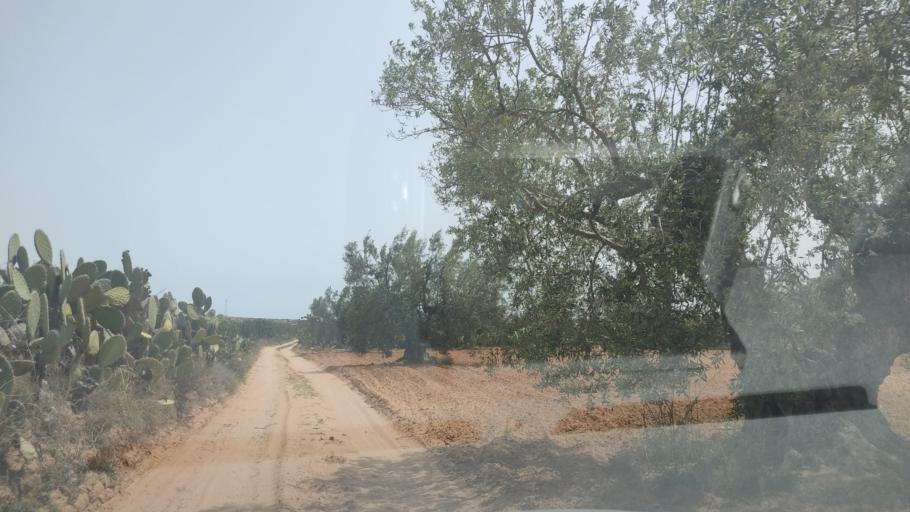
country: TN
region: Safaqis
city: Sfax
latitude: 34.8346
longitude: 10.5994
